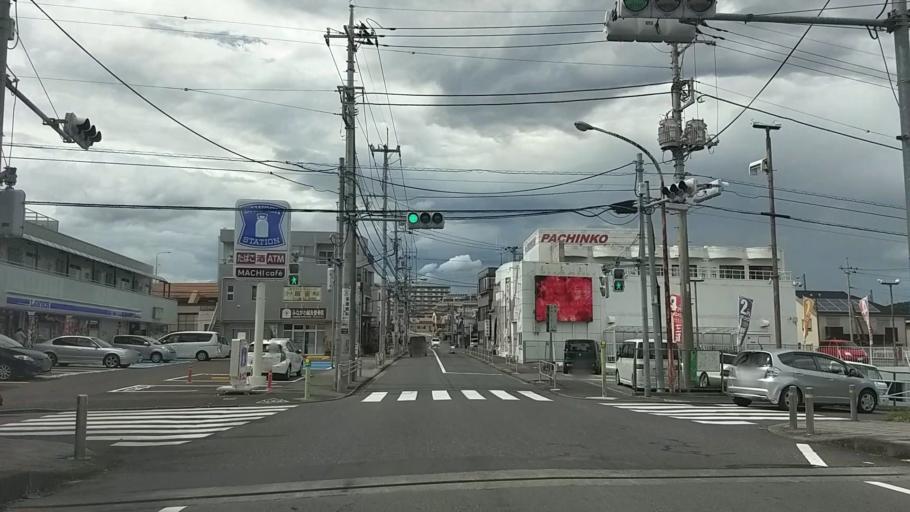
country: JP
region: Tokyo
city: Hachioji
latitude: 35.6533
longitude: 139.3001
